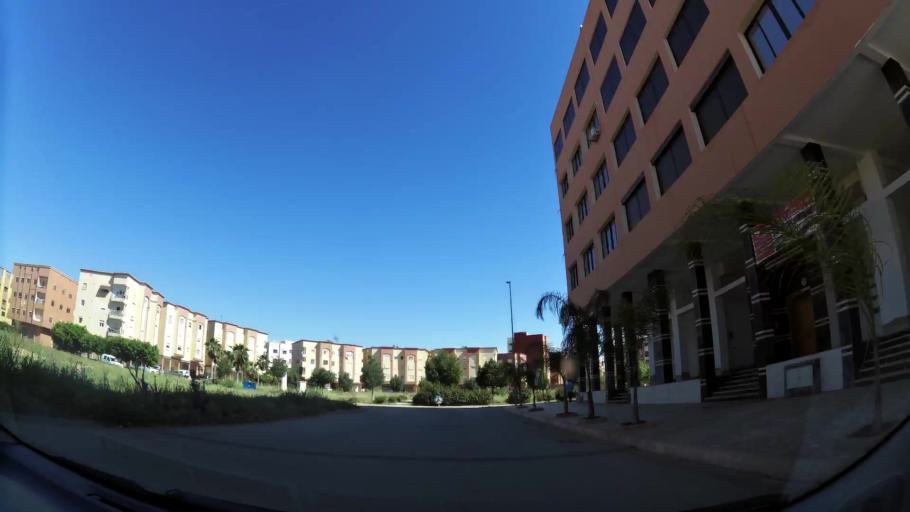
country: MA
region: Oriental
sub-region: Berkane-Taourirt
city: Berkane
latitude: 34.9423
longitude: -2.3320
